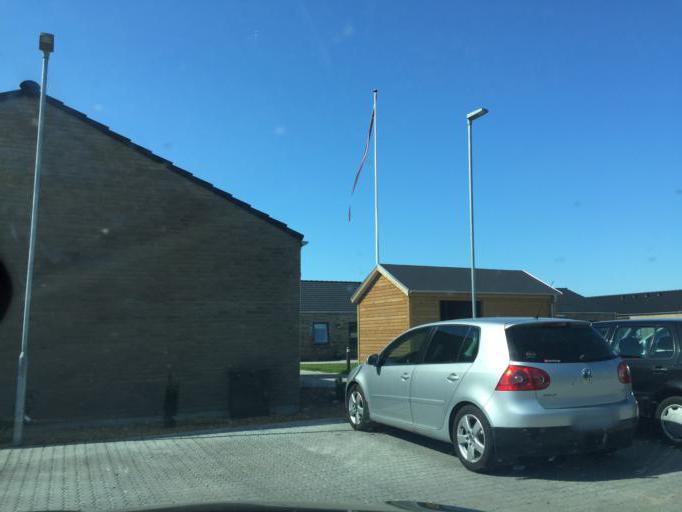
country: DK
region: South Denmark
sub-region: Kerteminde Kommune
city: Langeskov
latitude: 55.3581
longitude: 10.5866
